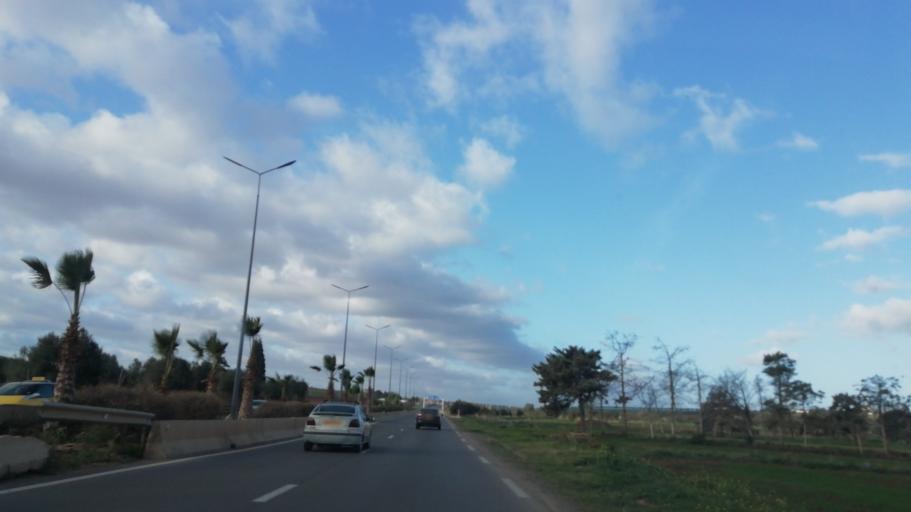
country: DZ
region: Ain Temouchent
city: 'Ain Temouchent
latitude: 35.3251
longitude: -1.1286
